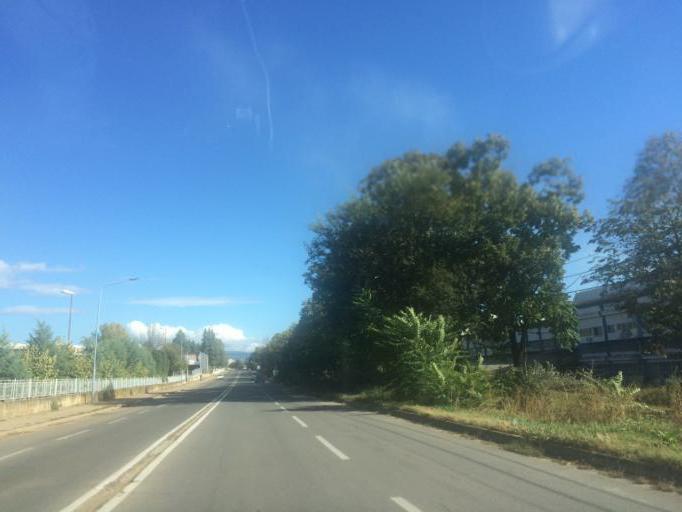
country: MK
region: Kocani
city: Orizari
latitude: 41.9138
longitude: 22.4307
